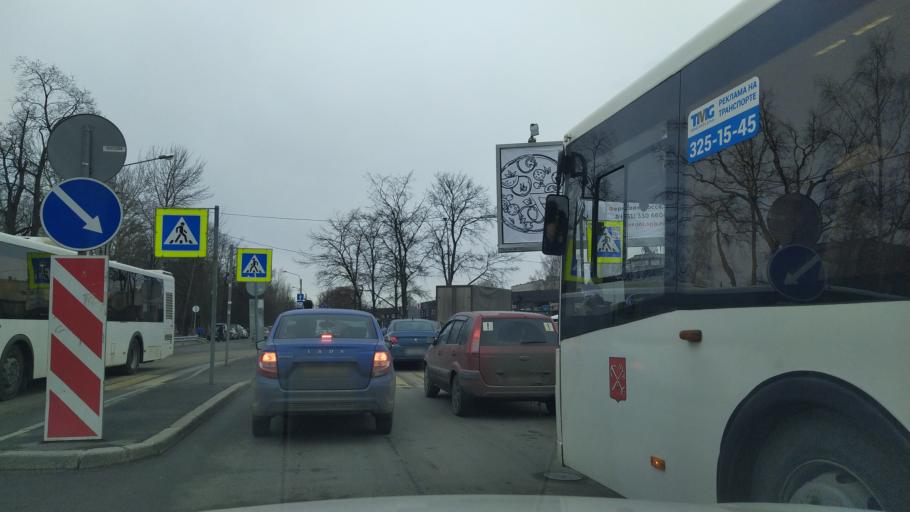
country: RU
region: Leningrad
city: Udel'naya
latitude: 60.0166
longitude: 30.3118
